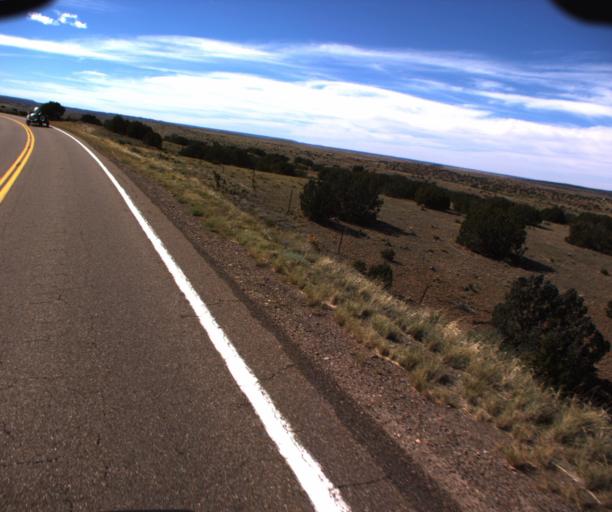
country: US
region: Arizona
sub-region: Apache County
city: Saint Johns
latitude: 34.4863
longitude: -109.5813
